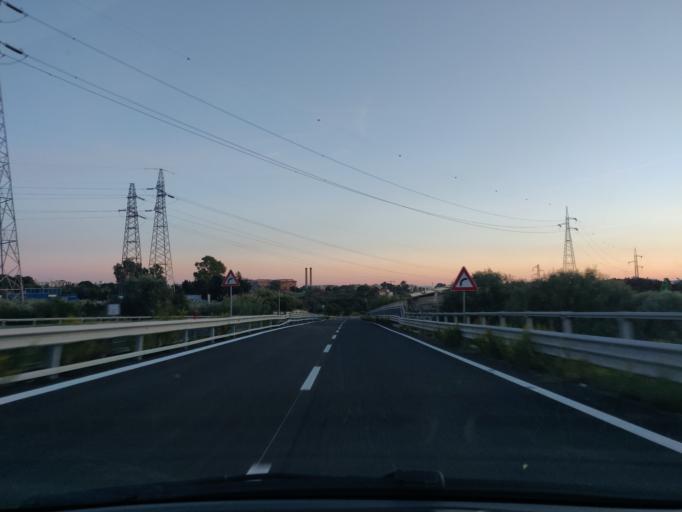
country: IT
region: Latium
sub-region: Citta metropolitana di Roma Capitale
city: Civitavecchia
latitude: 42.1109
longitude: 11.7925
